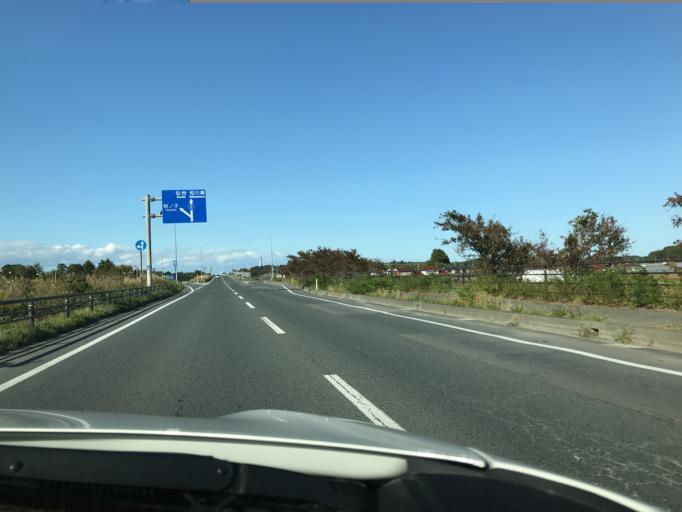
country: JP
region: Miyagi
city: Marumori
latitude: 37.7984
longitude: 140.9438
